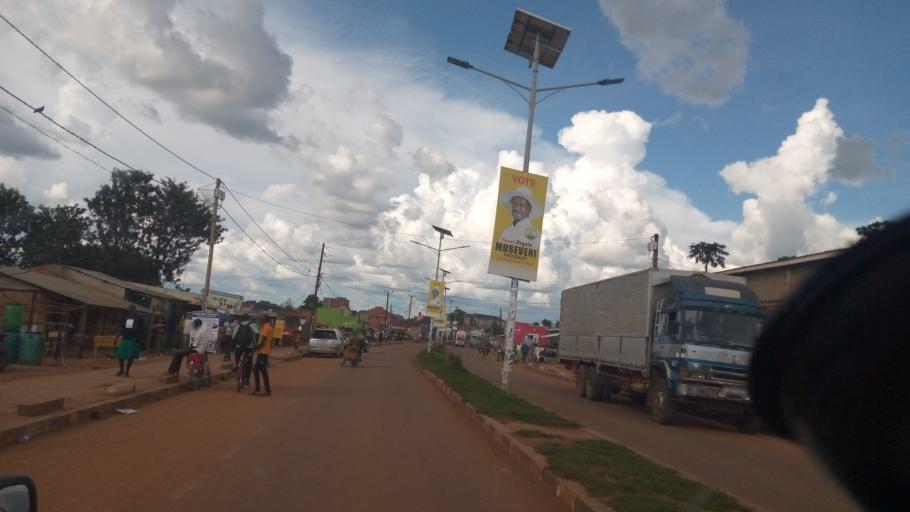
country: UG
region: Northern Region
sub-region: Lira District
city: Lira
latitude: 2.2412
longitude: 32.8893
